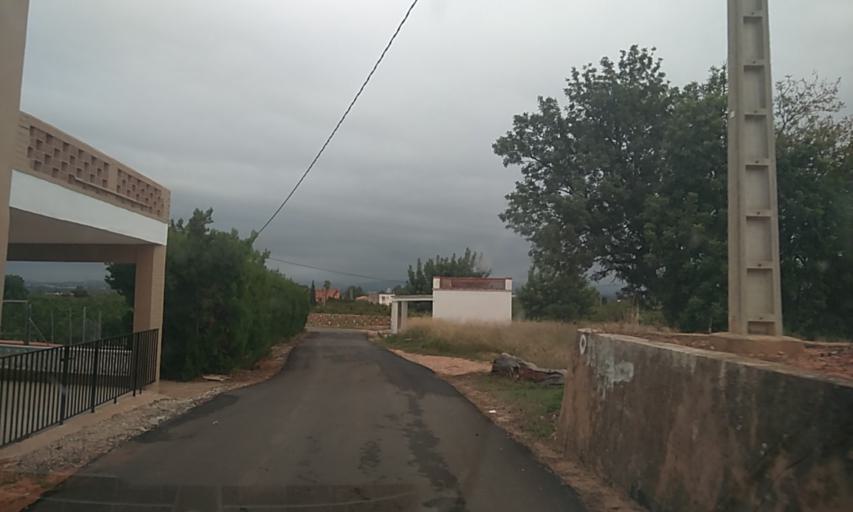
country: ES
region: Valencia
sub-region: Provincia de Valencia
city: Benimodo
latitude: 39.1933
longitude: -0.5622
